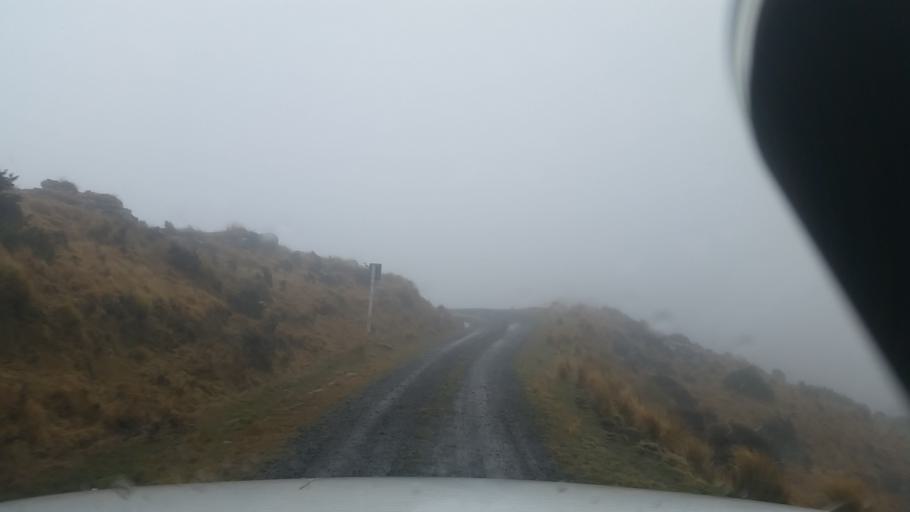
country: NZ
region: Canterbury
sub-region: Christchurch City
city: Christchurch
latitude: -43.8388
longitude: 172.8700
